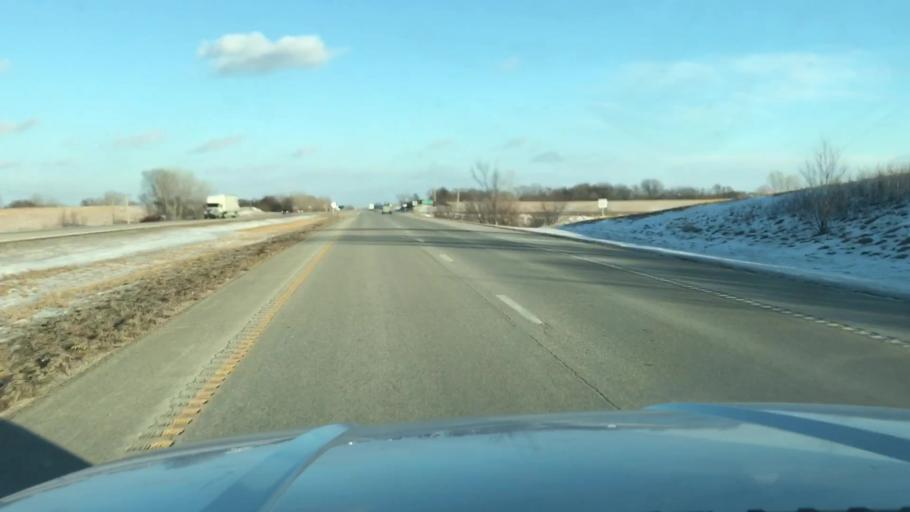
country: US
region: Missouri
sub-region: Clinton County
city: Gower
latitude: 39.7472
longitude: -94.6457
